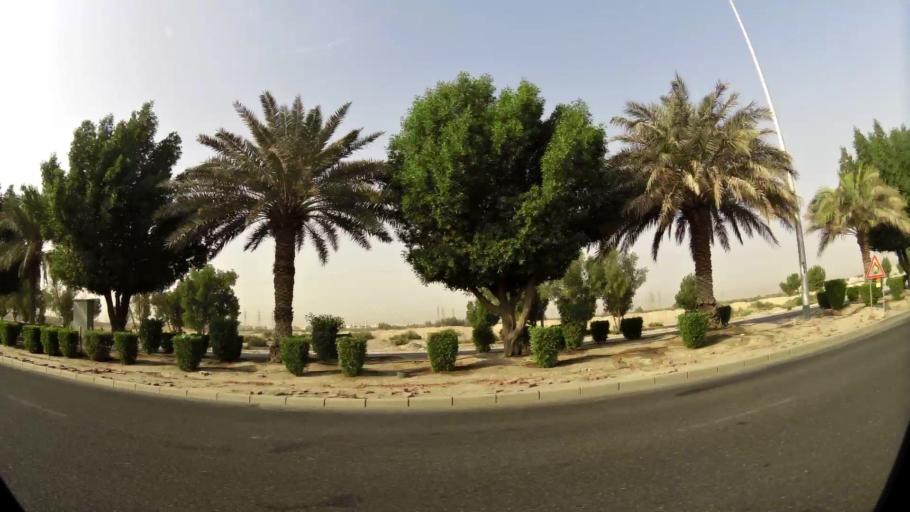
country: KW
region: Al Asimah
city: Ar Rabiyah
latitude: 29.3182
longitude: 47.8048
